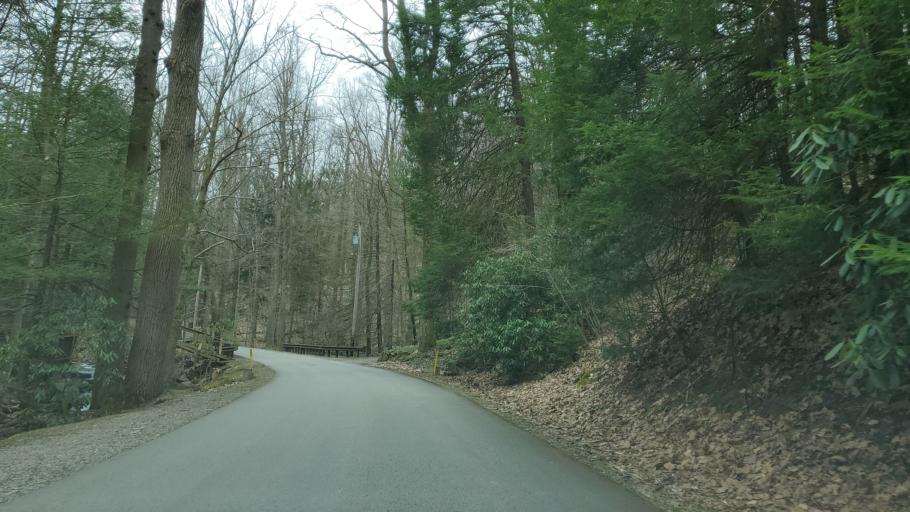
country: US
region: Pennsylvania
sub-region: Westmoreland County
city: Ligonier
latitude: 40.1594
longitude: -79.2324
